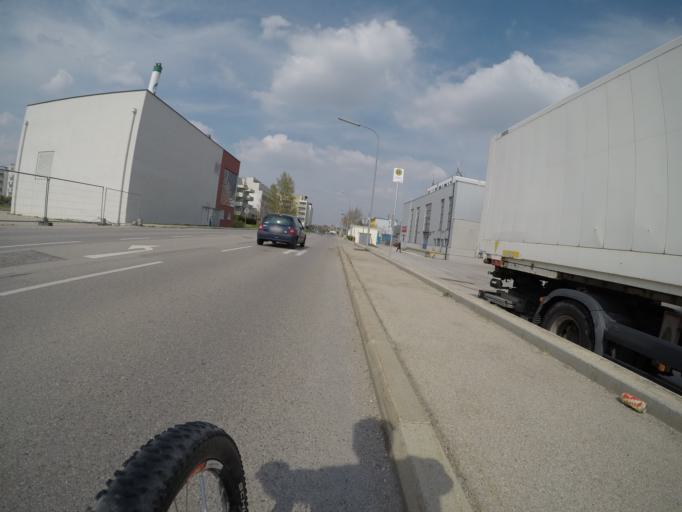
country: AT
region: Lower Austria
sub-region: Politischer Bezirk Modling
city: Wiener Neudorf
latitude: 48.0760
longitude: 16.3107
